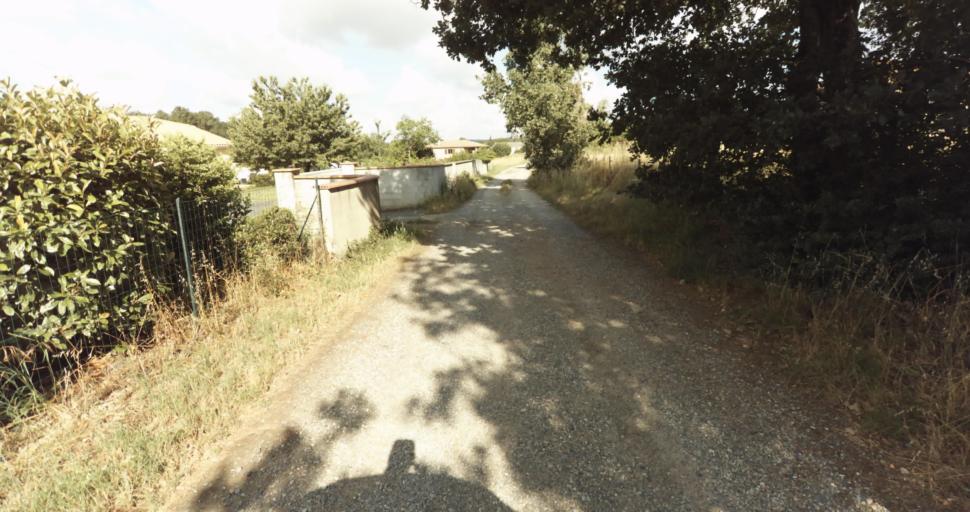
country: FR
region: Midi-Pyrenees
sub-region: Departement de la Haute-Garonne
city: Fontenilles
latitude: 43.5616
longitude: 1.2096
